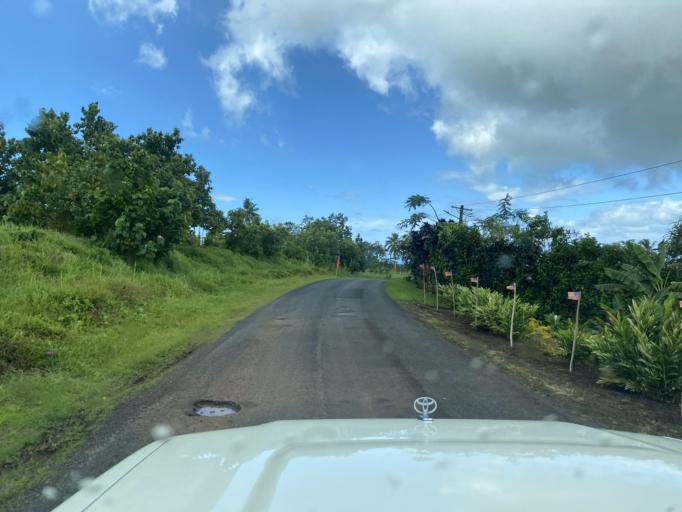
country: WS
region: Va`a-o-Fonoti
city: Samamea
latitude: -13.9736
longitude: -171.5829
